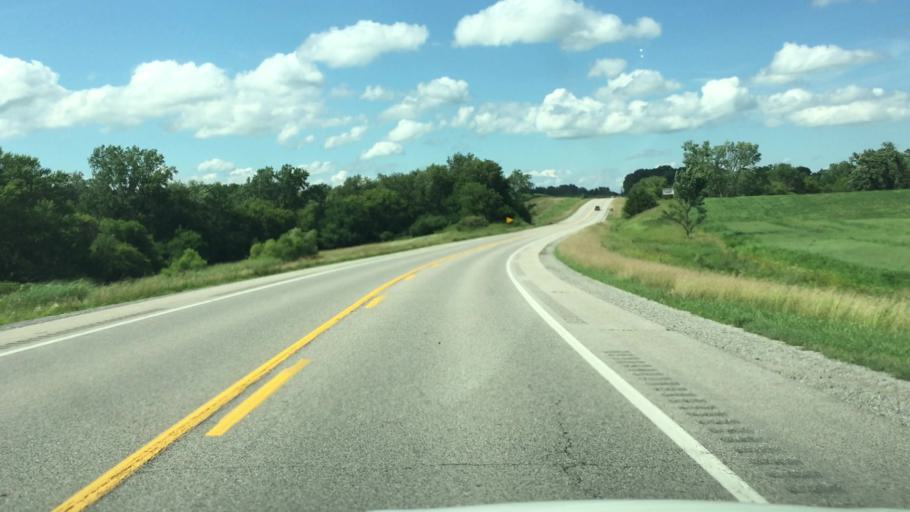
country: US
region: Iowa
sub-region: Johnson County
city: Solon
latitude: 41.7672
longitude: -91.4828
